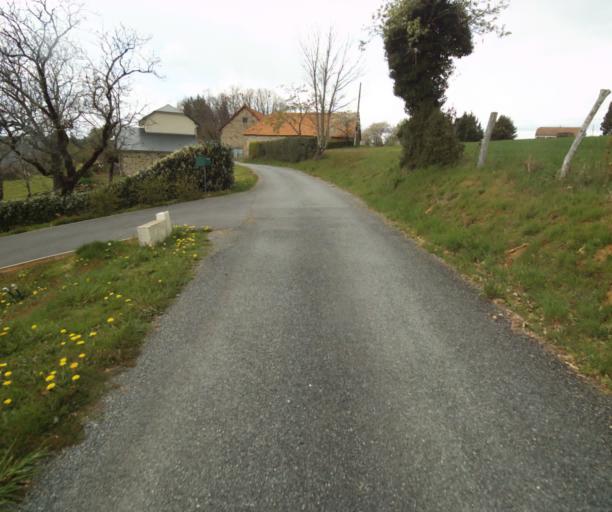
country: FR
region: Limousin
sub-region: Departement de la Correze
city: Naves
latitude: 45.3055
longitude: 1.8112
